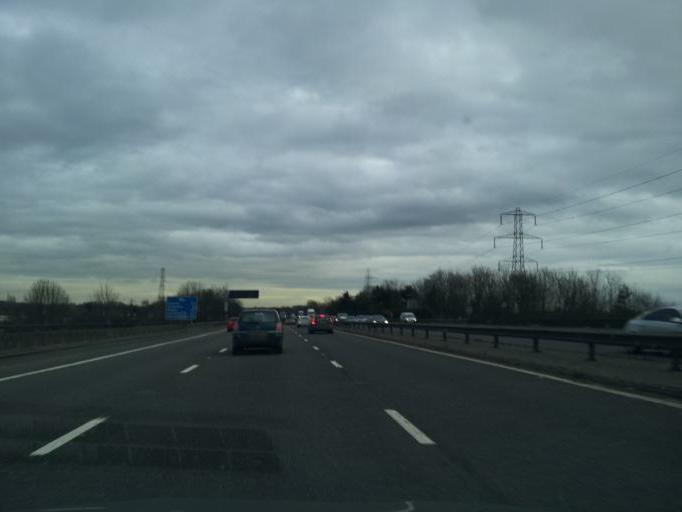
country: GB
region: England
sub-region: Warwickshire
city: Exhall
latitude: 52.4569
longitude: -1.4804
